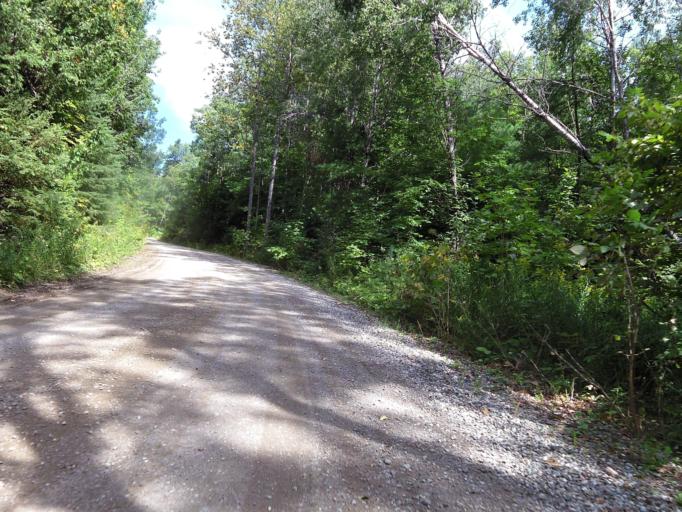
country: CA
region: Ontario
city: Renfrew
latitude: 45.1231
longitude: -76.7196
